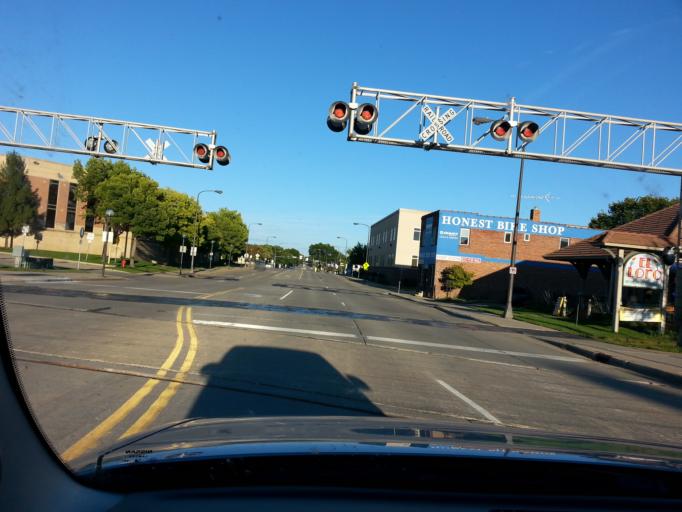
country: US
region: Minnesota
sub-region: Olmsted County
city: Rochester
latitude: 44.0193
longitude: -92.4618
